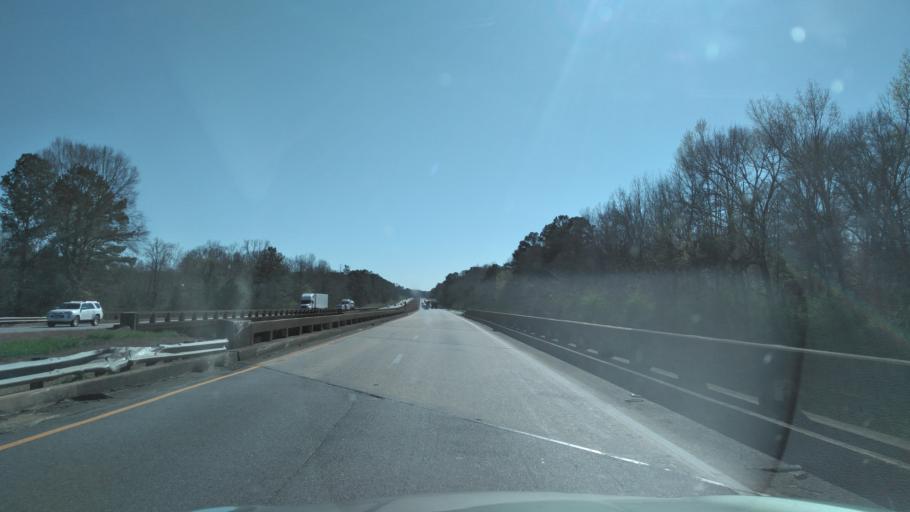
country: US
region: Alabama
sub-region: Butler County
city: Greenville
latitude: 31.8949
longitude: -86.6016
